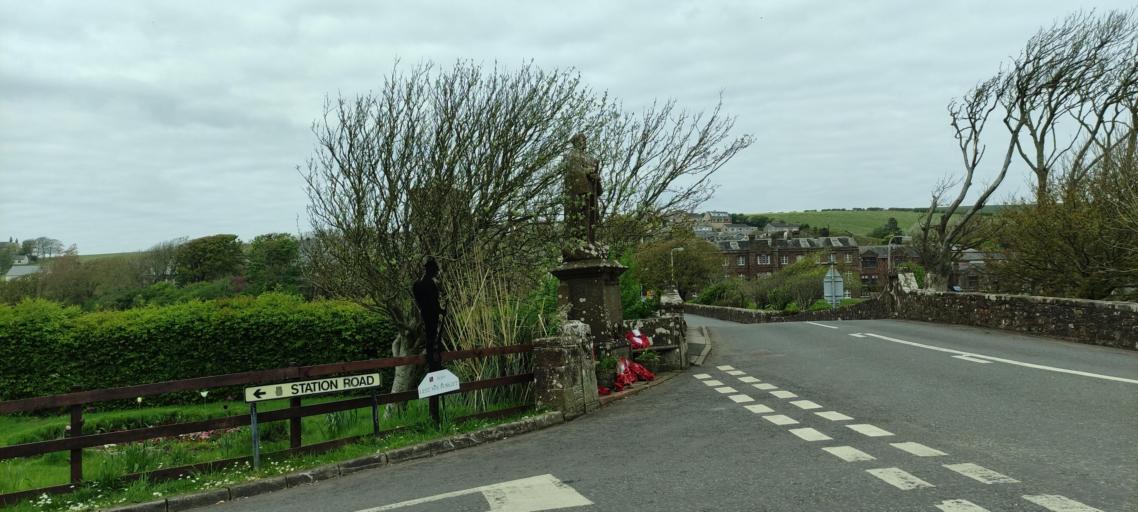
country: GB
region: England
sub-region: Cumbria
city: Saint Bees
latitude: 54.4929
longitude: -3.5913
